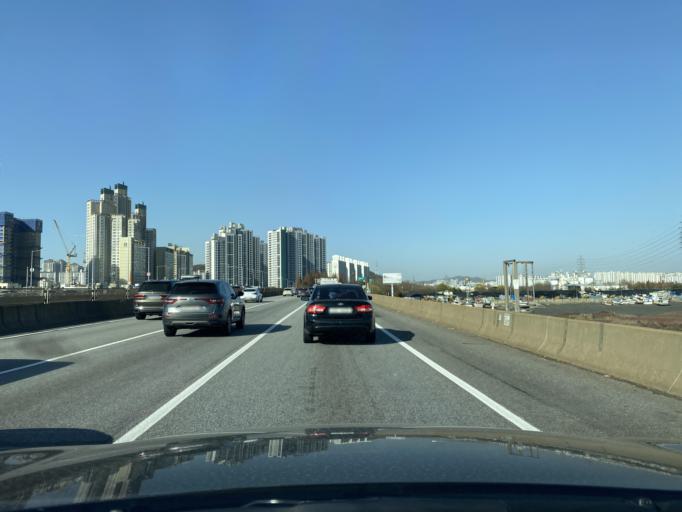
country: KR
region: Incheon
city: Incheon
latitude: 37.3974
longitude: 126.7426
